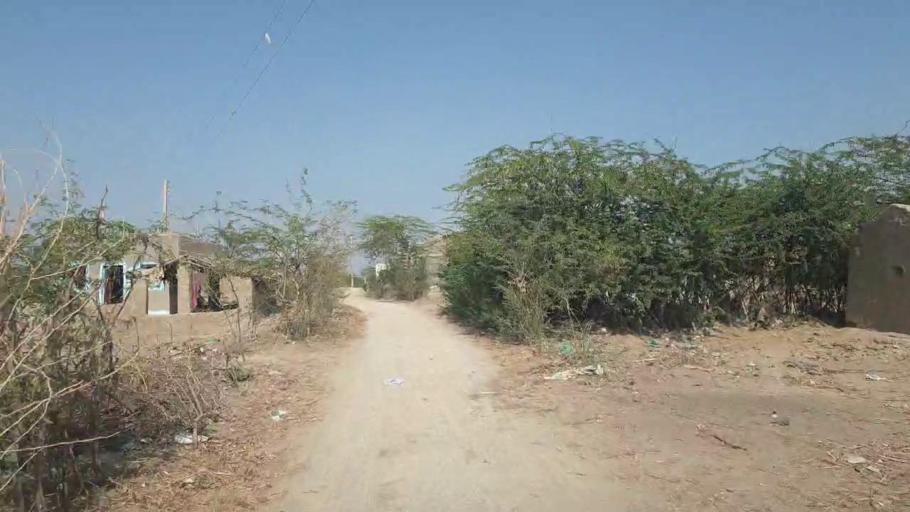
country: PK
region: Sindh
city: Dhoro Naro
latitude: 25.5126
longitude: 69.5603
